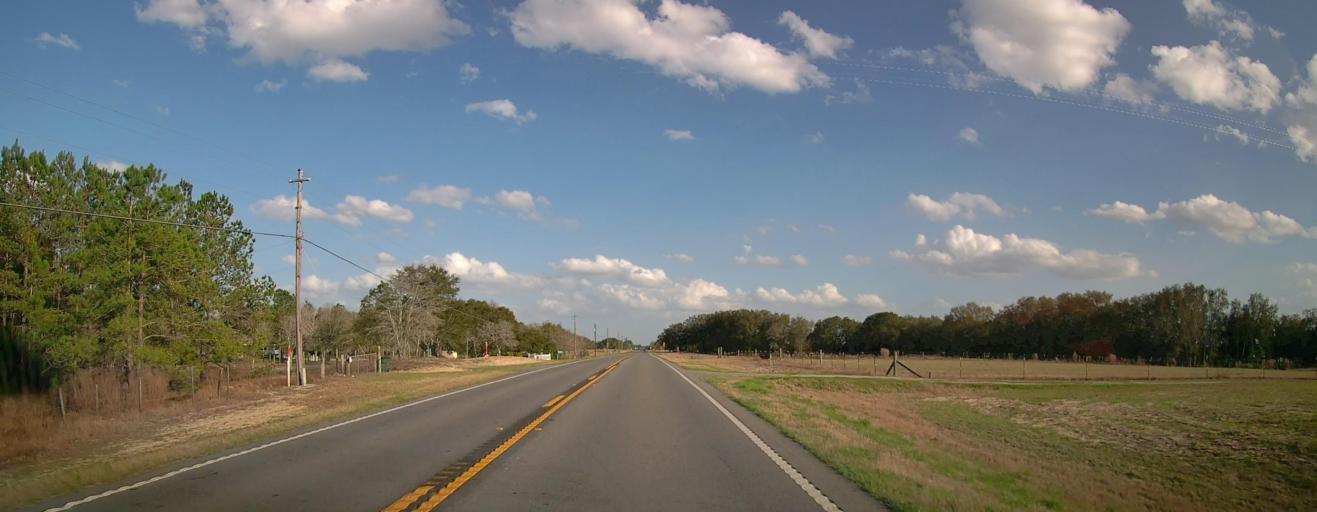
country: US
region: Georgia
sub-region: Tattnall County
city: Reidsville
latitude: 32.1044
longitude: -82.1687
